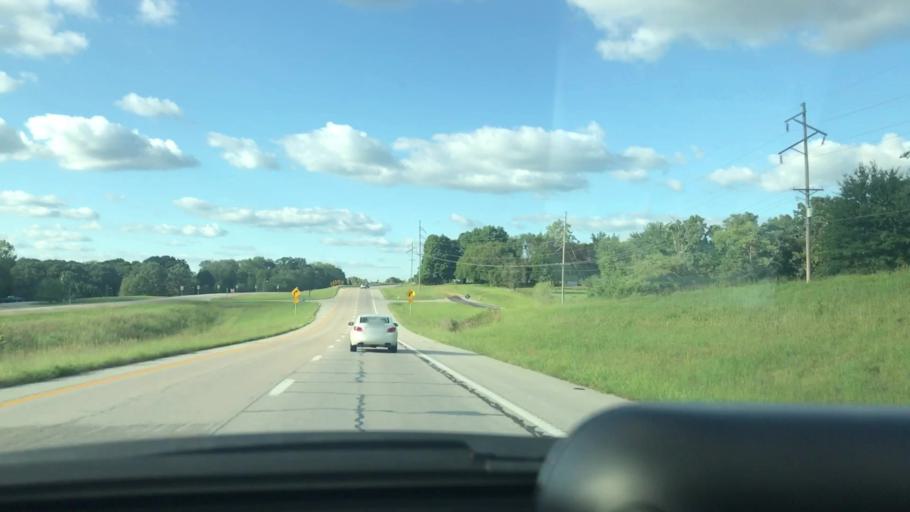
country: US
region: Missouri
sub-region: Pettis County
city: Sedalia
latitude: 38.6321
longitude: -93.2672
